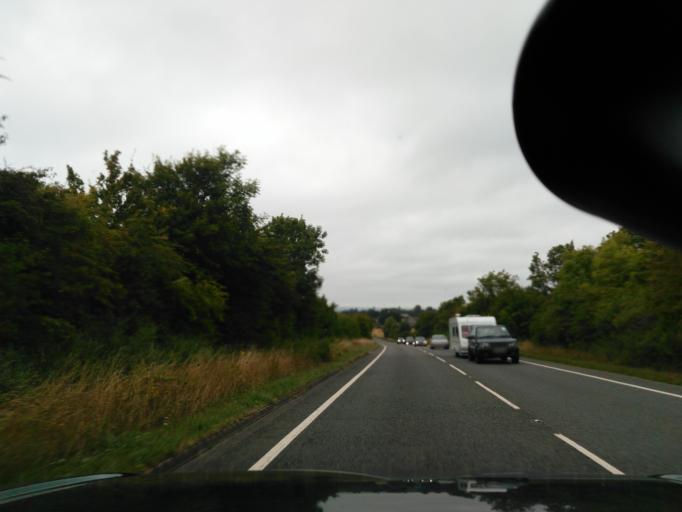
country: GB
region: England
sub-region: Wiltshire
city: Upton Scudamore
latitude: 51.2381
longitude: -2.1879
